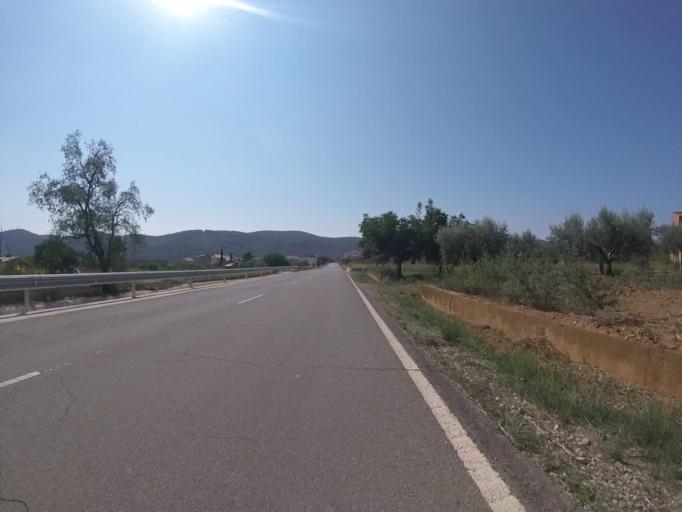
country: ES
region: Valencia
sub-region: Provincia de Castello
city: Adzaneta
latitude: 40.2235
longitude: -0.1729
